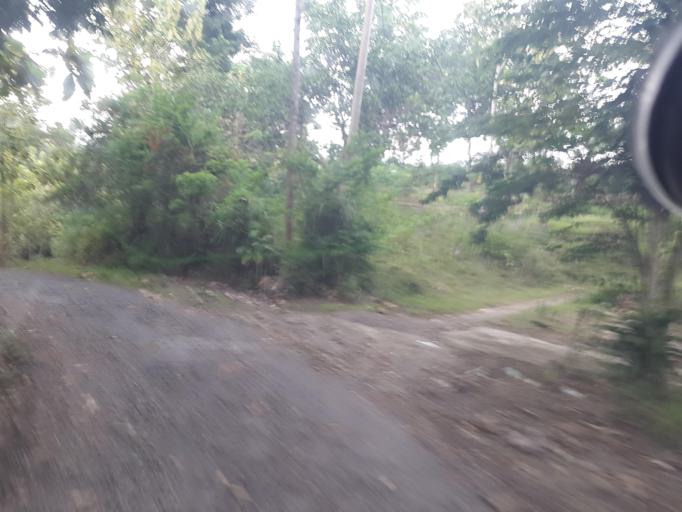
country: ID
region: East Java
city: Ponorogo
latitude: -7.7316
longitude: 111.3100
